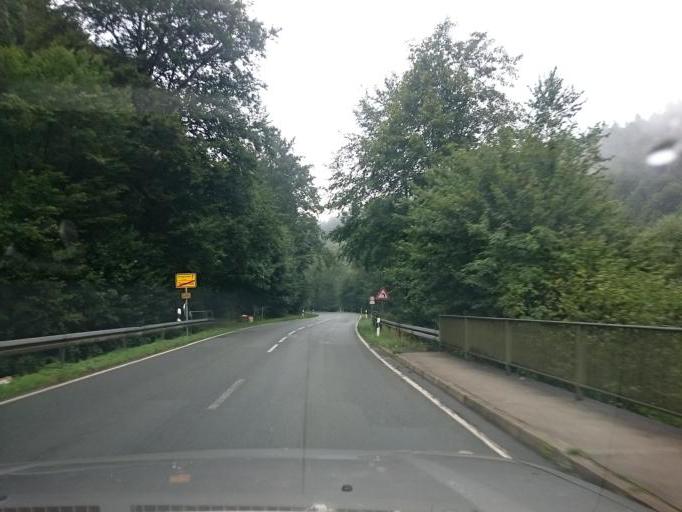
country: DE
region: Bavaria
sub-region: Upper Franconia
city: Gossweinstein
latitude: 49.7853
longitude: 11.3561
